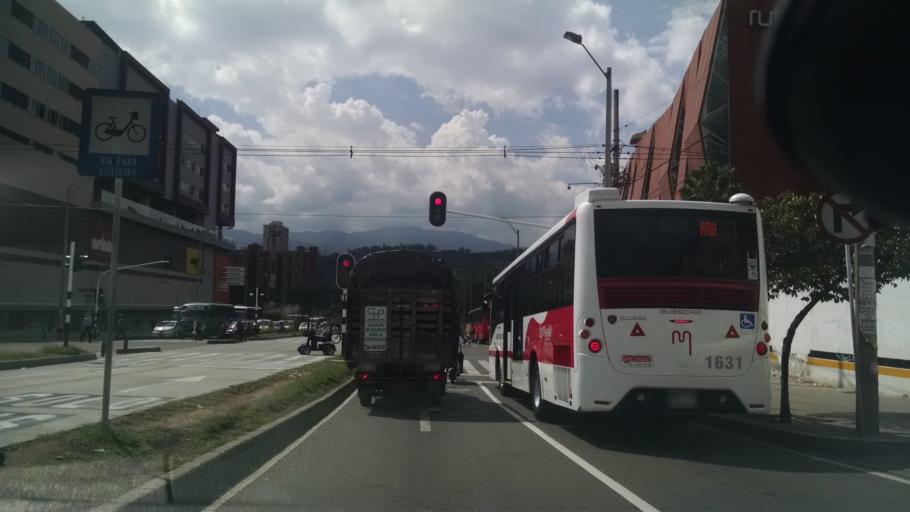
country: CO
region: Antioquia
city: Medellin
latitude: 6.2644
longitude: -75.5660
